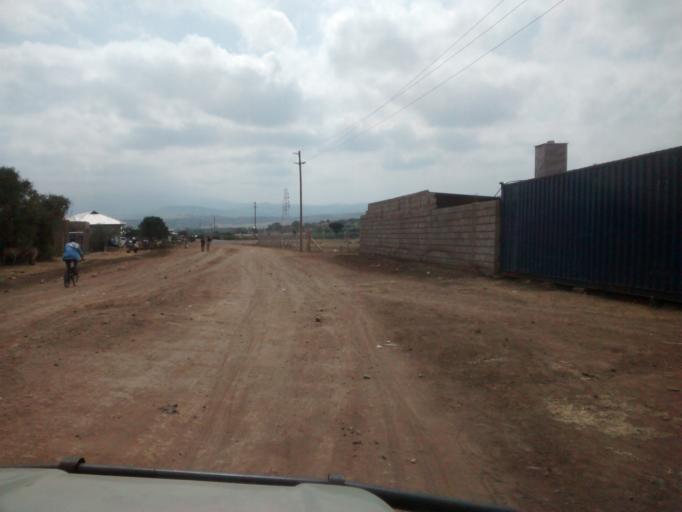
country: TZ
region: Arusha
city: Arusha
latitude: -3.3869
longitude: 36.5902
